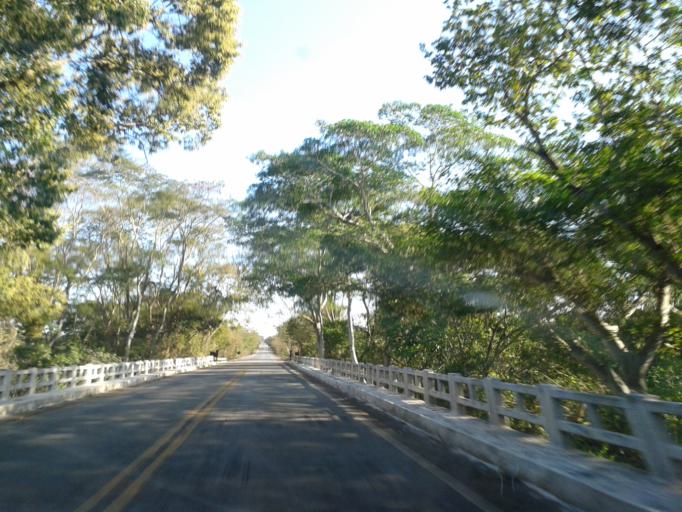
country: BR
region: Goias
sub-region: Itapuranga
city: Itapuranga
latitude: -15.3476
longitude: -50.4082
